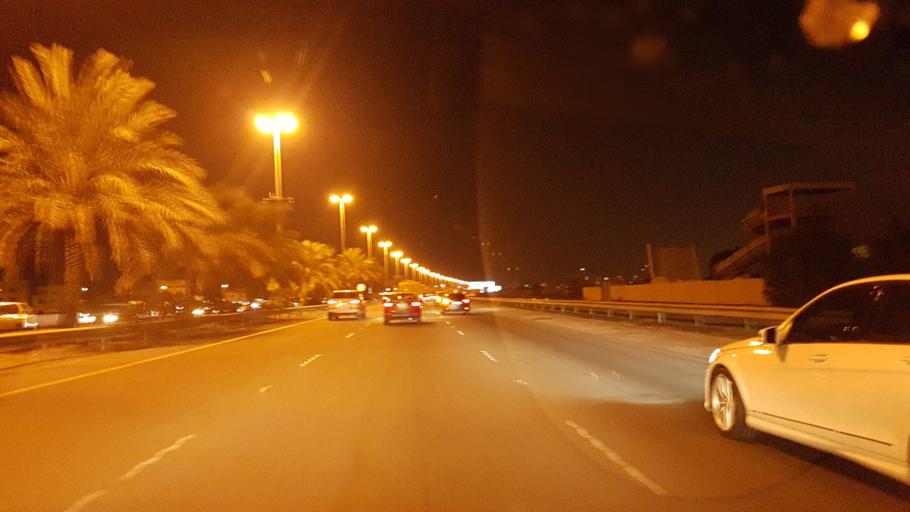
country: BH
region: Northern
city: Madinat `Isa
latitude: 26.1955
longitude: 50.5074
